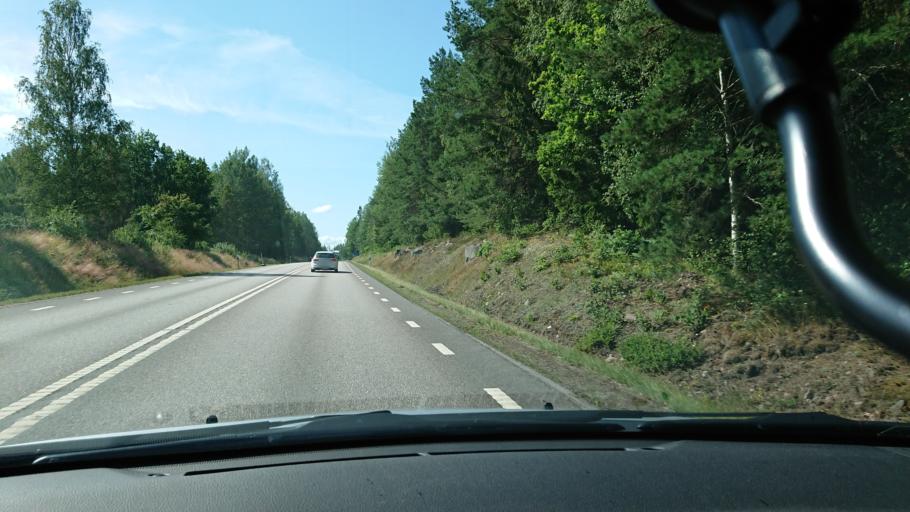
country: SE
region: Kalmar
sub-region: Vimmerby Kommun
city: Sodra Vi
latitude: 57.8528
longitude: 15.7483
